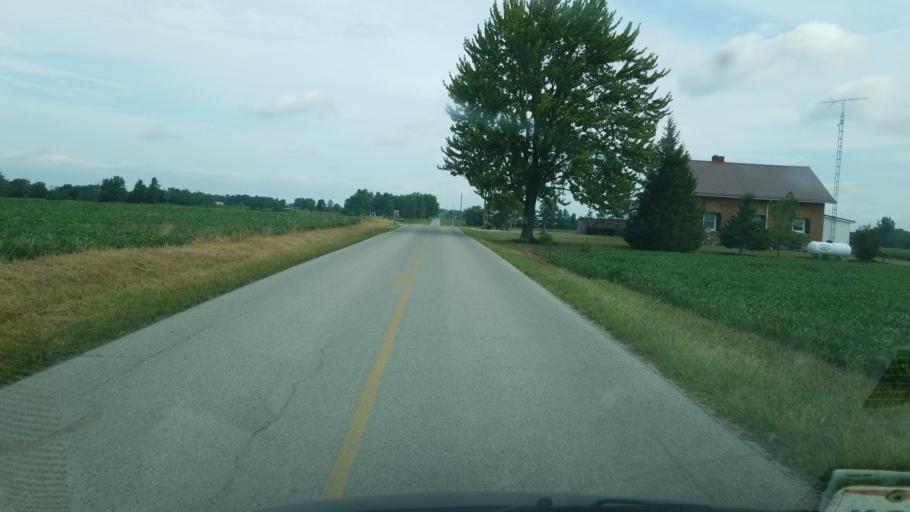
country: US
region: Ohio
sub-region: Seneca County
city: Tiffin
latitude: 41.0990
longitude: -83.0930
